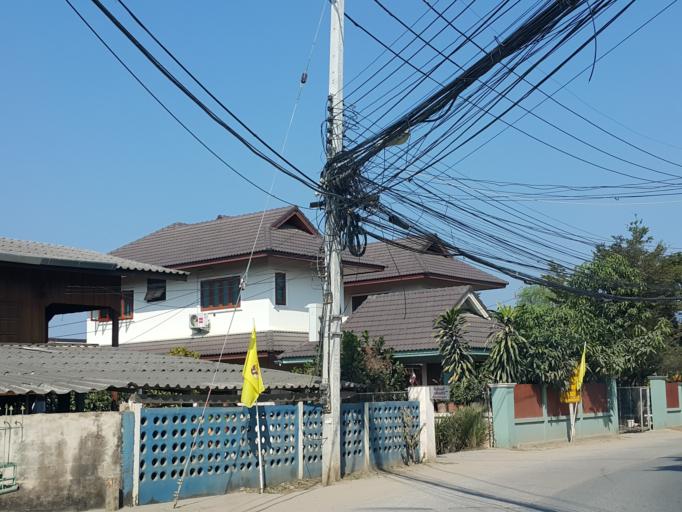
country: TH
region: Chiang Mai
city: San Sai
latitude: 18.8448
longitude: 99.0183
